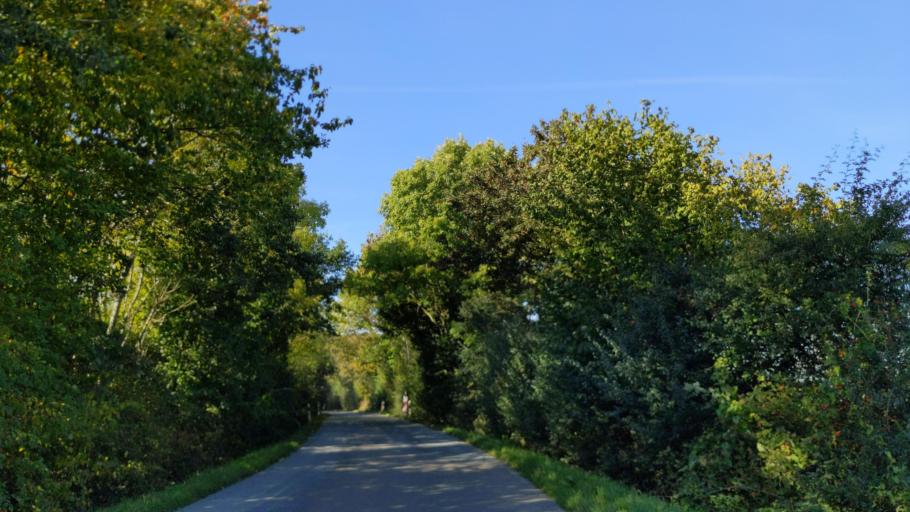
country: DE
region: Schleswig-Holstein
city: Ahrensbok
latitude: 53.9974
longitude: 10.6302
